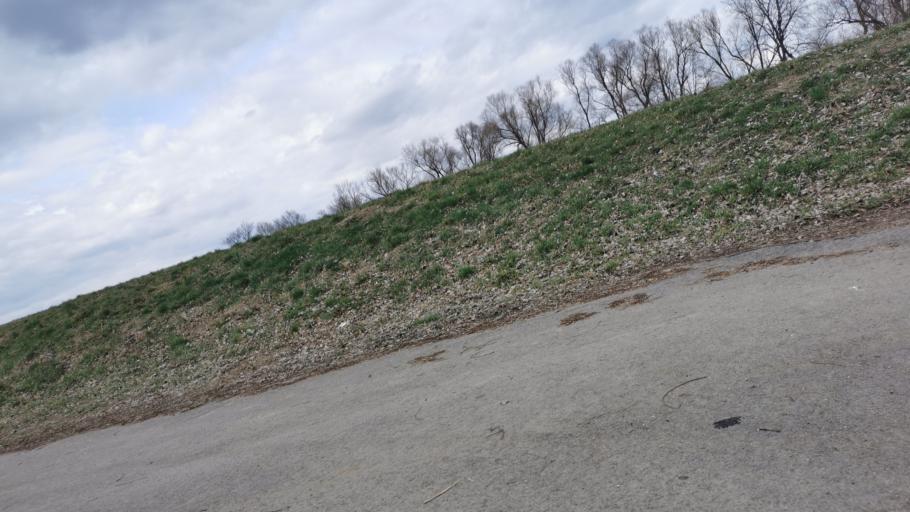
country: CZ
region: South Moravian
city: Rohatec
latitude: 48.8729
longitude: 17.2110
